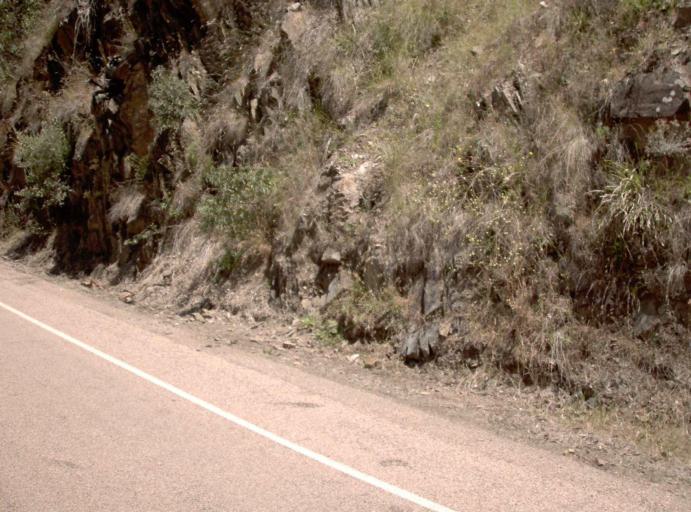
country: AU
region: Victoria
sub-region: East Gippsland
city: Bairnsdale
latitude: -37.4669
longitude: 147.8299
